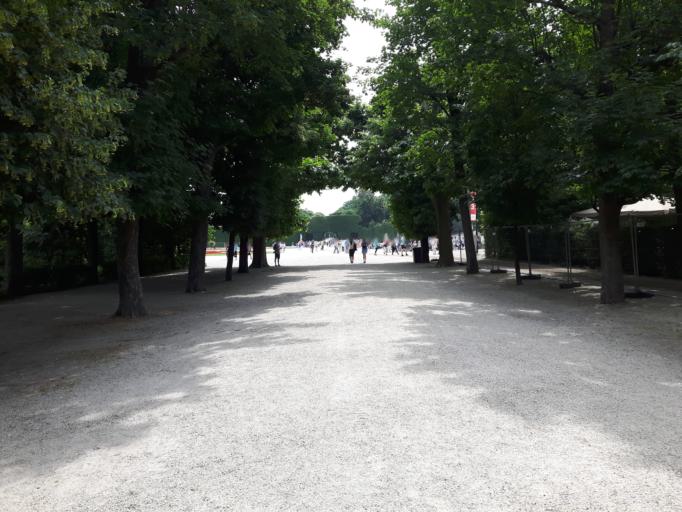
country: AT
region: Vienna
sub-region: Wien Stadt
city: Vienna
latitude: 48.1821
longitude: 16.3090
